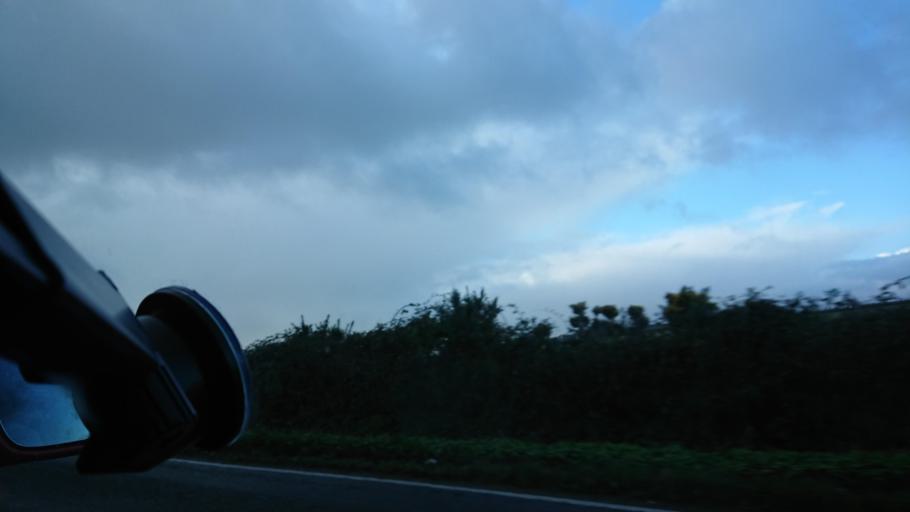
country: GB
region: England
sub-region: Cornwall
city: Looe
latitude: 50.3511
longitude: -4.4758
